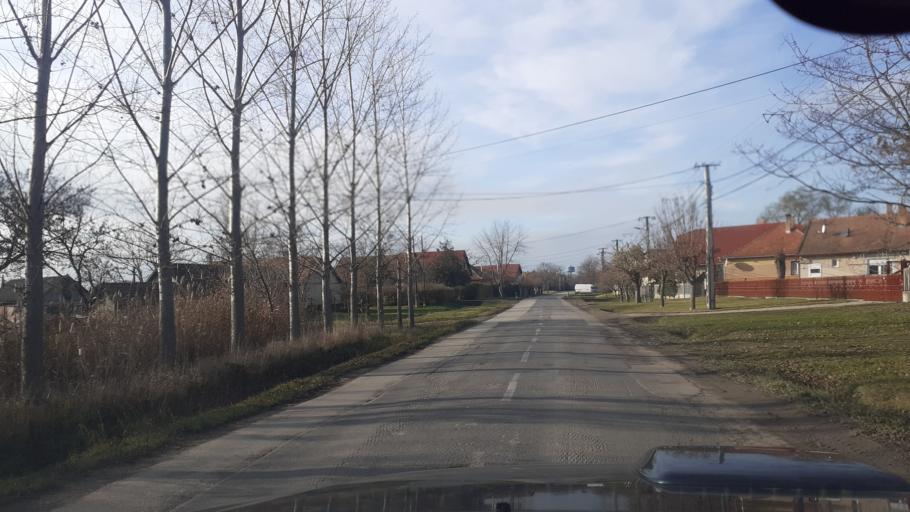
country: HU
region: Pest
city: Domsod
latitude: 47.0905
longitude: 19.0273
